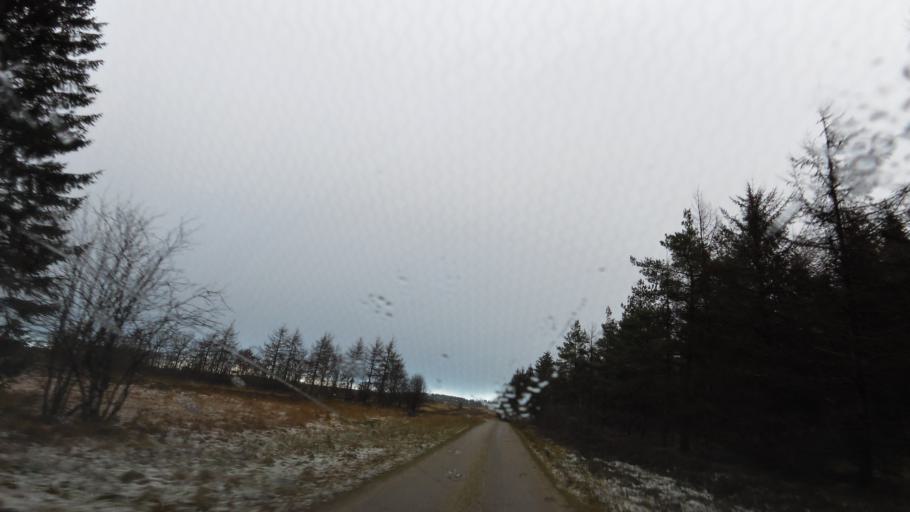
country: DK
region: Central Jutland
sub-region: Ikast-Brande Kommune
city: Brande
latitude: 56.0180
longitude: 9.1611
